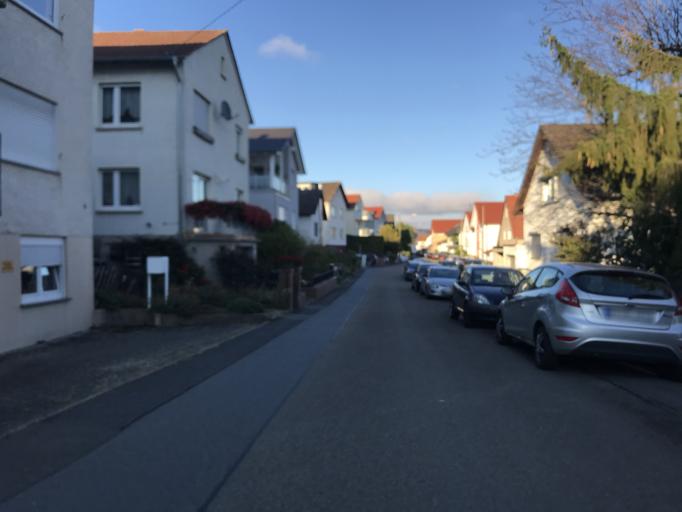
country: DE
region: Rheinland-Pfalz
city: Ober-Olm
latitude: 49.9374
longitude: 8.1946
